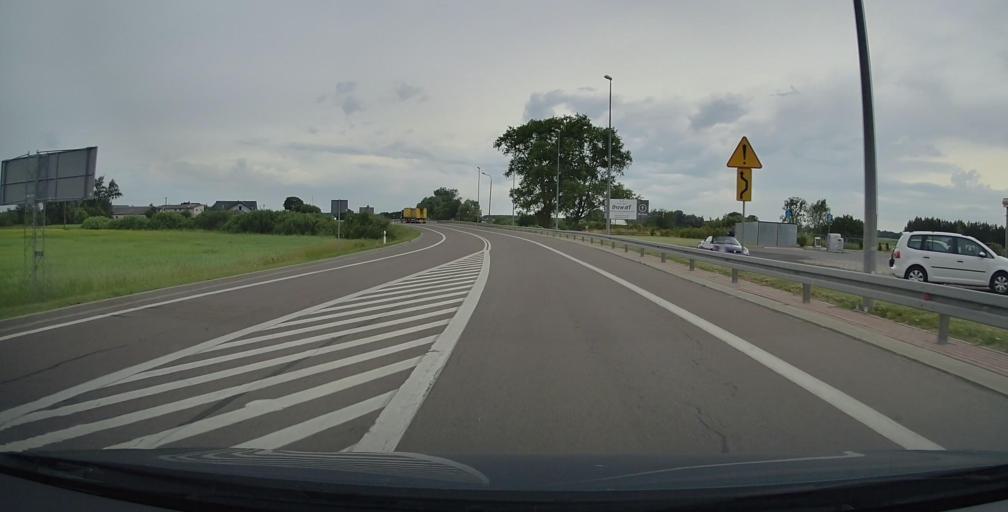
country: PL
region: Lublin Voivodeship
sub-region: Powiat bialski
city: Terespol
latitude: 52.0625
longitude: 23.5839
